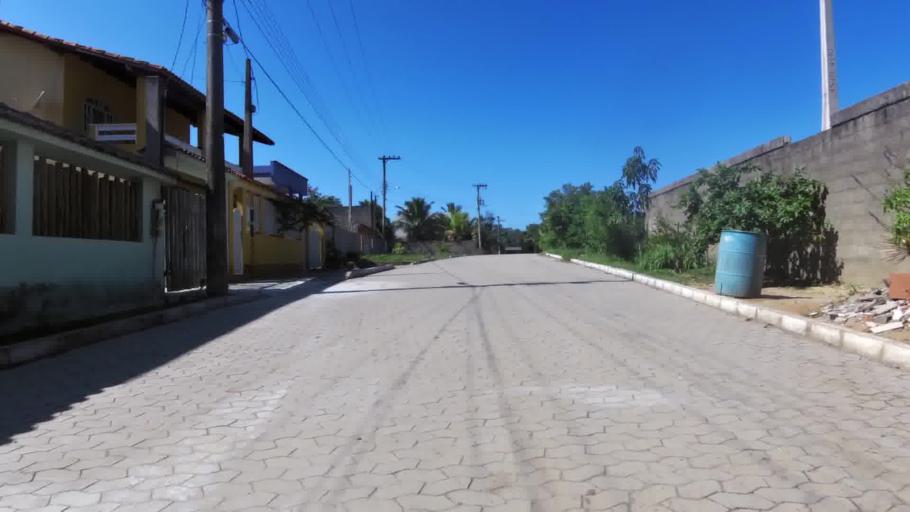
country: BR
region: Espirito Santo
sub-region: Piuma
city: Piuma
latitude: -20.8290
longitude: -40.6258
